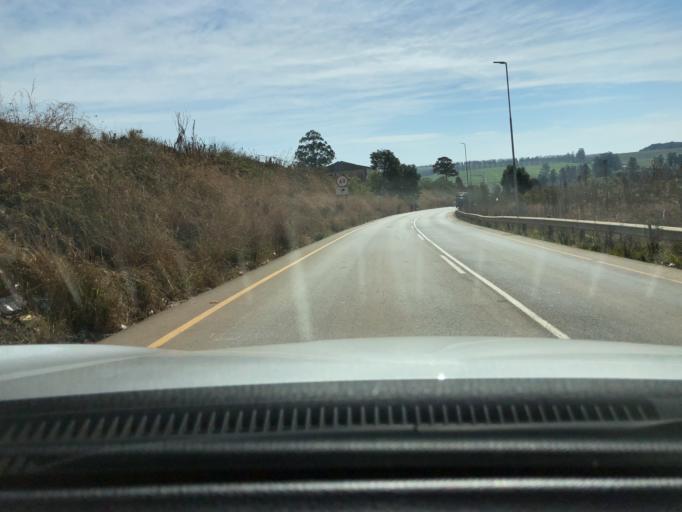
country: ZA
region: KwaZulu-Natal
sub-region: Sisonke District Municipality
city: Ixopo
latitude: -30.1504
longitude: 30.0660
